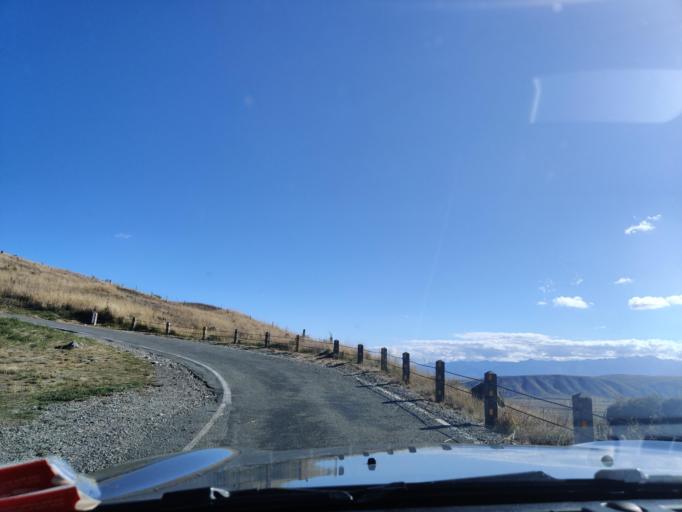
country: NZ
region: Canterbury
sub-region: Timaru District
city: Pleasant Point
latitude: -43.9826
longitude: 170.4656
